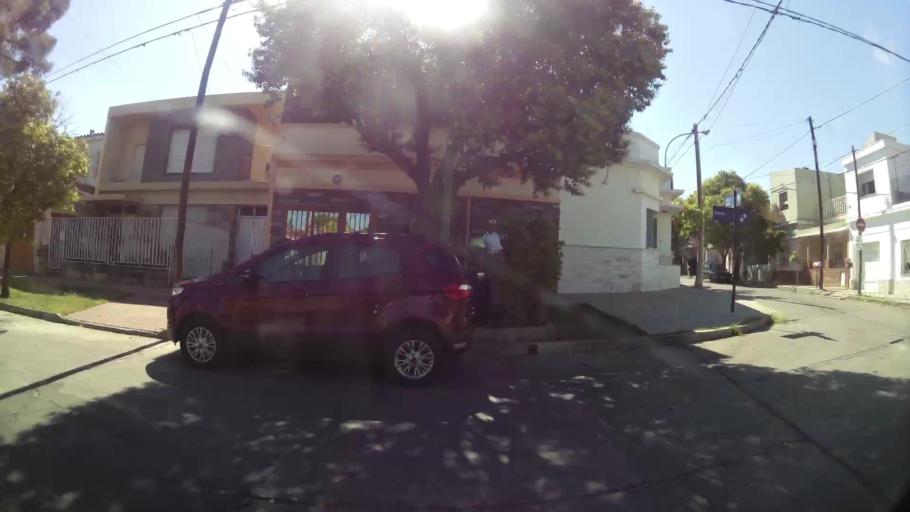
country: AR
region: Cordoba
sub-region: Departamento de Capital
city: Cordoba
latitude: -31.4174
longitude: -64.1621
